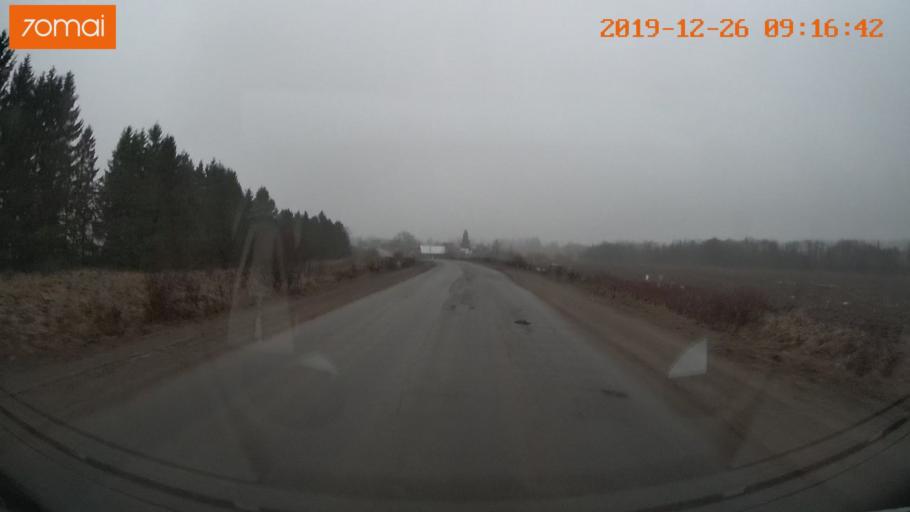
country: RU
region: Vologda
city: Gryazovets
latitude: 58.9215
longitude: 40.2392
